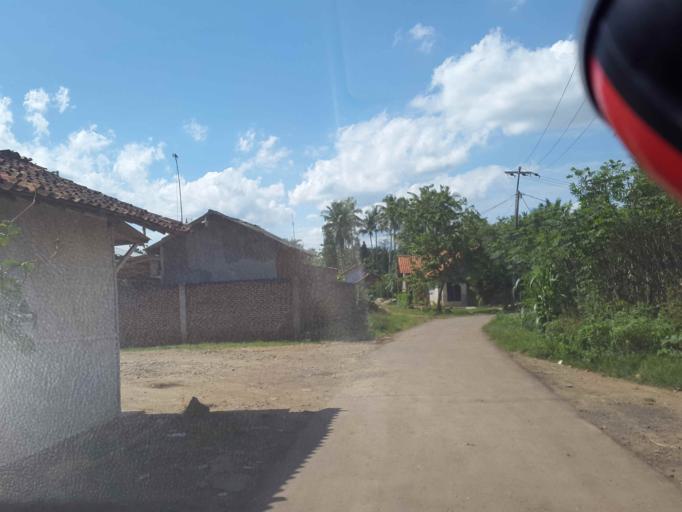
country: ID
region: Lampung
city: Natar
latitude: -5.3130
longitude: 105.1851
